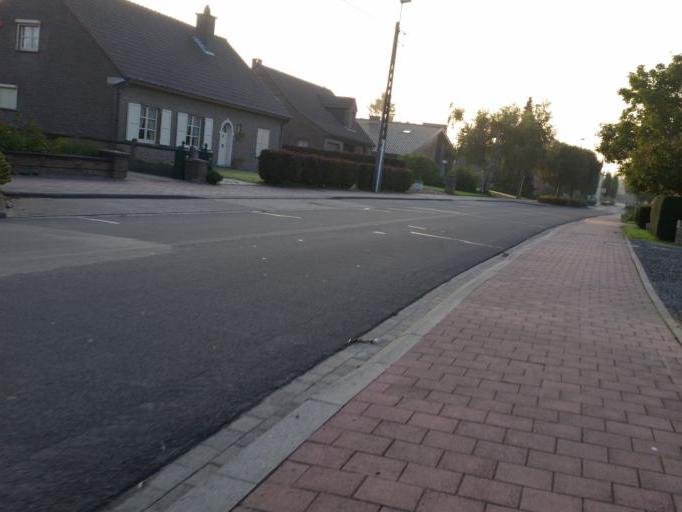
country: BE
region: Flanders
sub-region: Provincie Vlaams-Brabant
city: Zemst
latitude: 50.9673
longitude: 4.4462
